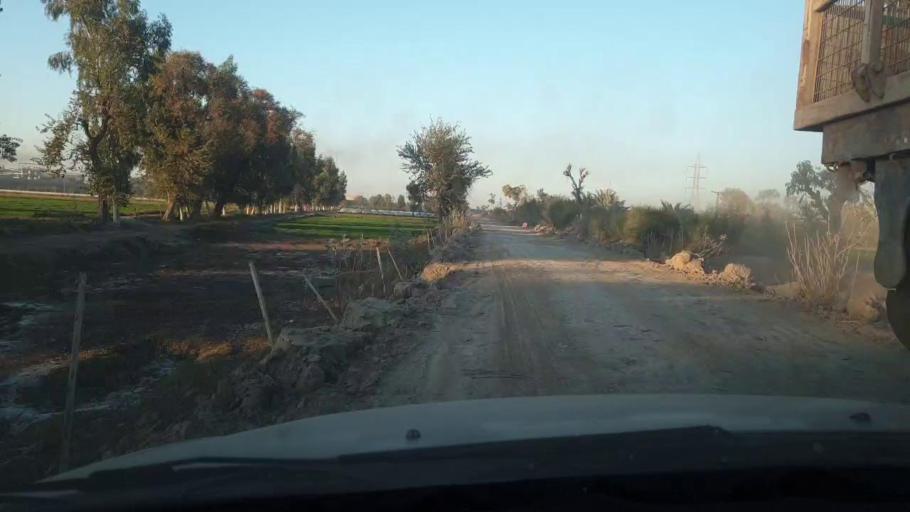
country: PK
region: Sindh
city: Ghotki
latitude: 28.0386
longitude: 69.3241
